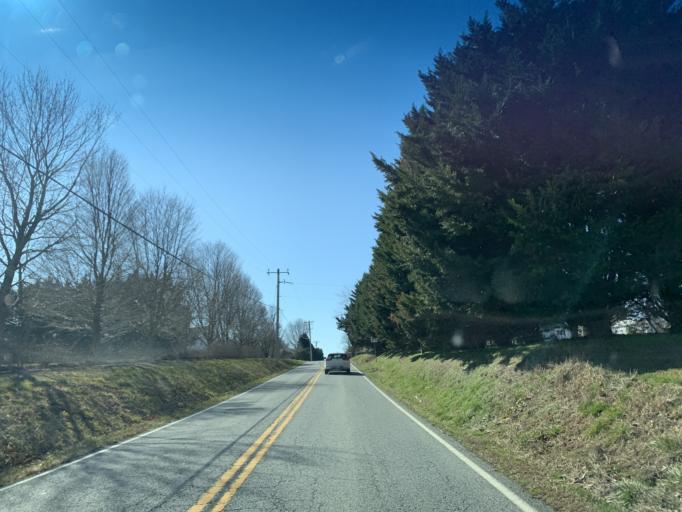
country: US
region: Maryland
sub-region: Cecil County
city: Charlestown
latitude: 39.4613
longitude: -75.8868
